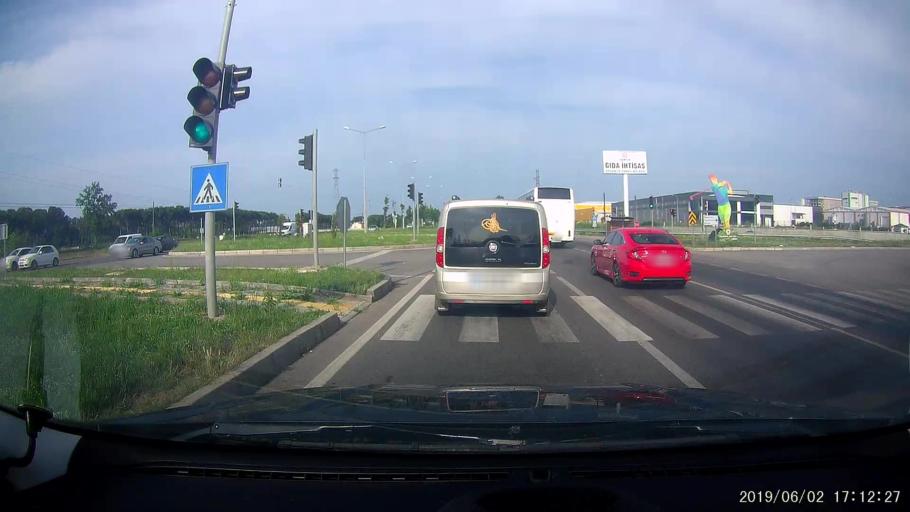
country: TR
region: Samsun
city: Tekkekoy
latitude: 41.2290
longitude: 36.4915
